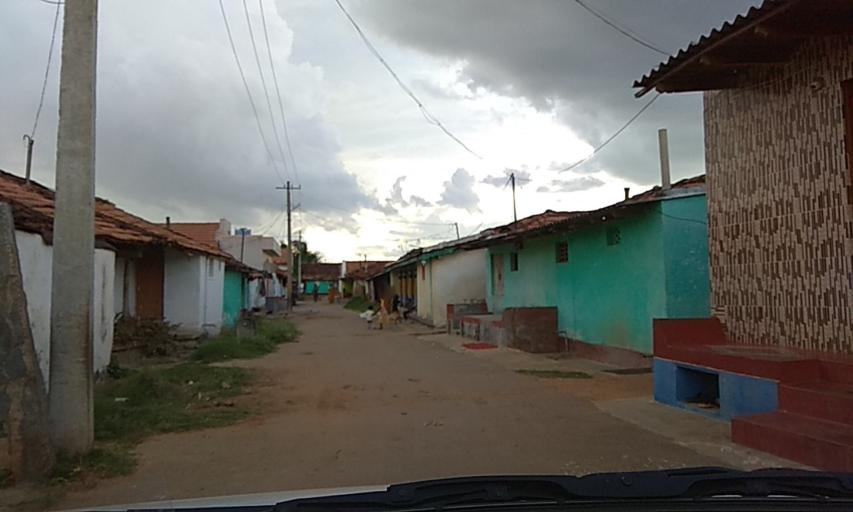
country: IN
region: Karnataka
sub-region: Chamrajnagar
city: Gundlupet
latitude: 11.8721
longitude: 76.7230
